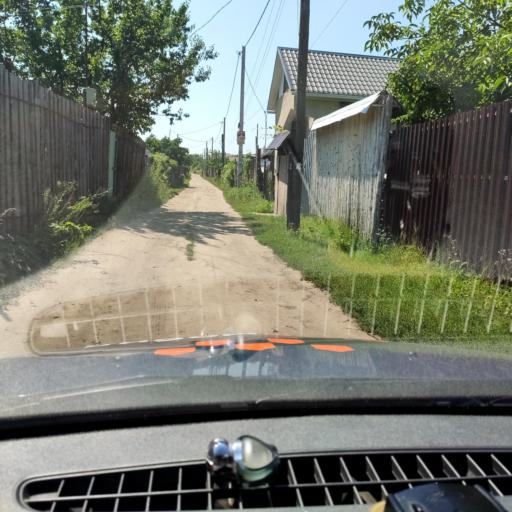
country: RU
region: Voronezj
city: Maslovka
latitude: 51.6002
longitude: 39.2330
